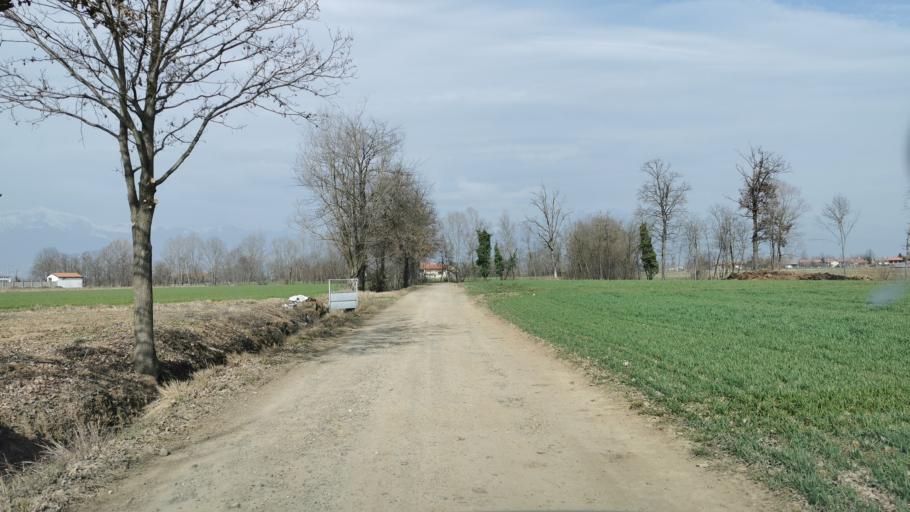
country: IT
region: Piedmont
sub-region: Provincia di Torino
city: Front
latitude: 45.2821
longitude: 7.6975
